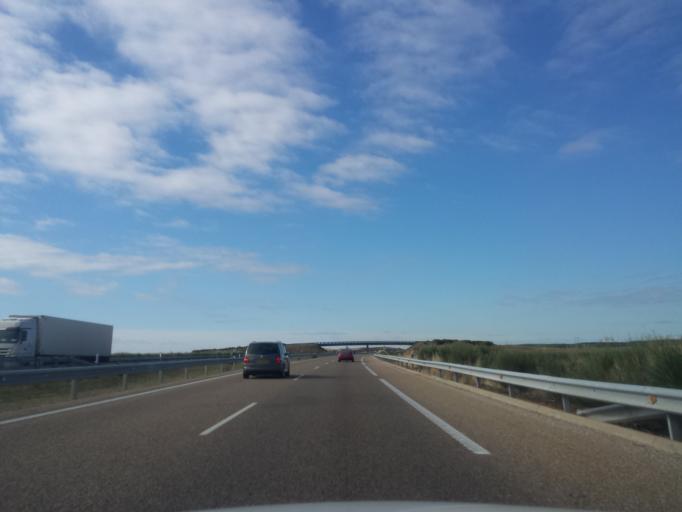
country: ES
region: Castille and Leon
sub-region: Provincia de Leon
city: Villademor de la Vega
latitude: 42.2688
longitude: -5.5906
